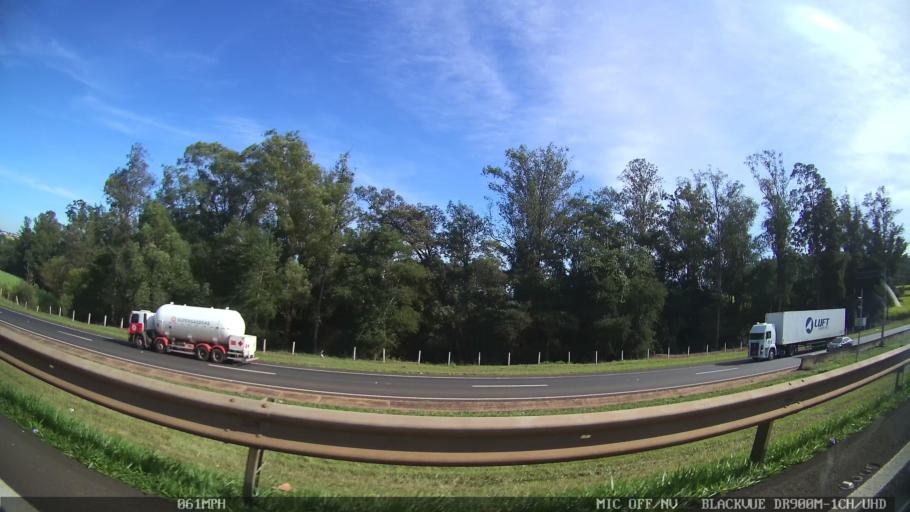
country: BR
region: Sao Paulo
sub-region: Araras
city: Araras
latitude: -22.3374
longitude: -47.3907
